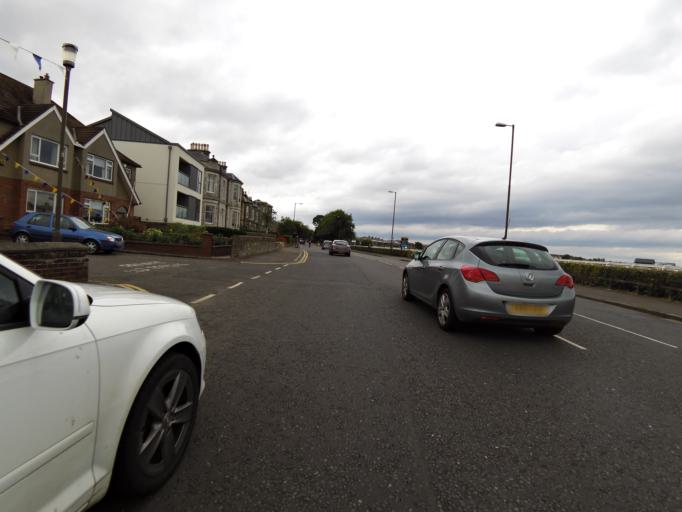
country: GB
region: Scotland
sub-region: East Lothian
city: Musselburgh
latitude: 55.9457
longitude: -3.0378
